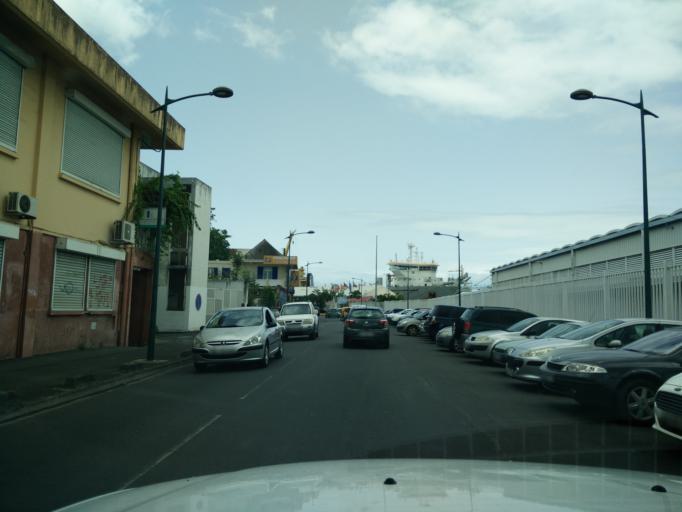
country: GP
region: Guadeloupe
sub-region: Guadeloupe
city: Pointe-a-Pitre
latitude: 16.2388
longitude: -61.5386
